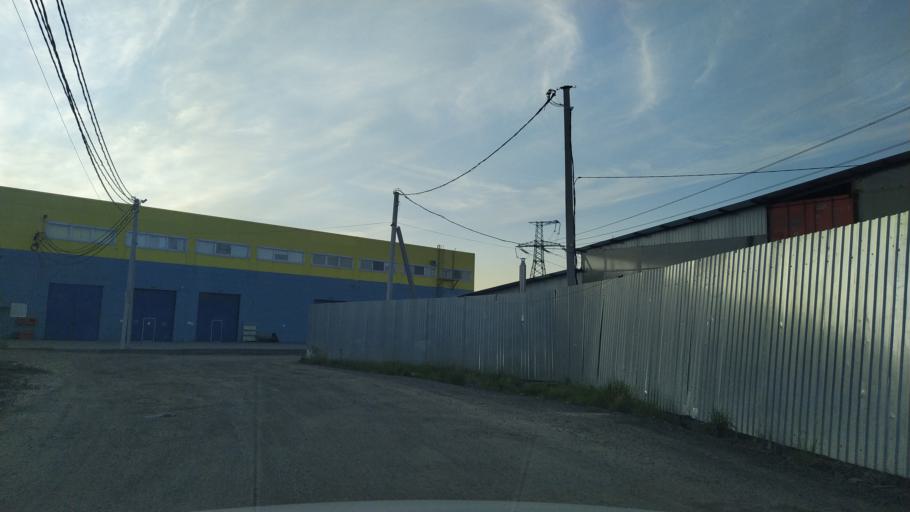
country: RU
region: St.-Petersburg
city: Obukhovo
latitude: 59.8059
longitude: 30.4593
